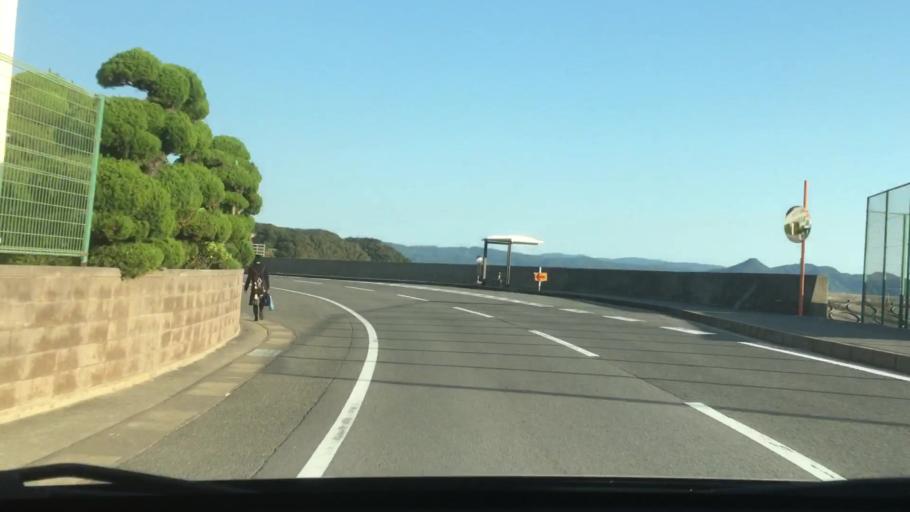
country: JP
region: Nagasaki
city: Sasebo
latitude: 33.0279
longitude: 129.5894
